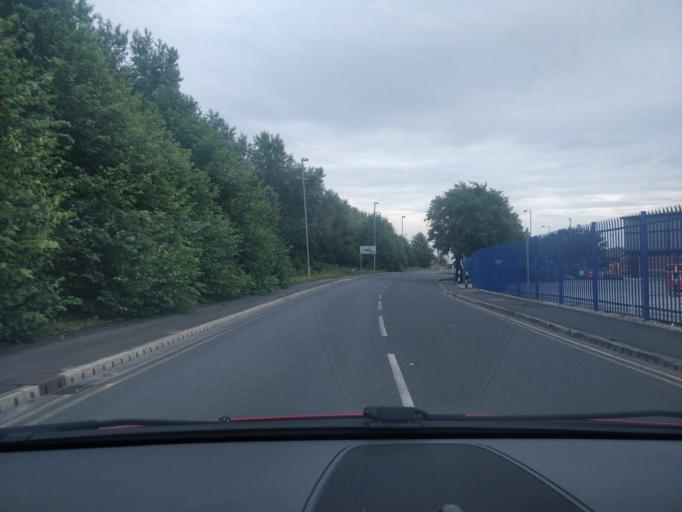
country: GB
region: England
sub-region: Sefton
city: Southport
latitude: 53.6355
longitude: -2.9680
